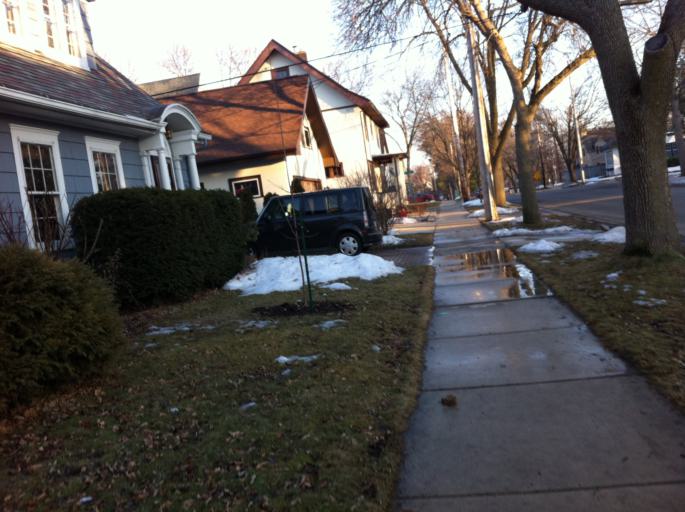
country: US
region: Wisconsin
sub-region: Dane County
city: Madison
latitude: 43.0641
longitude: -89.4231
